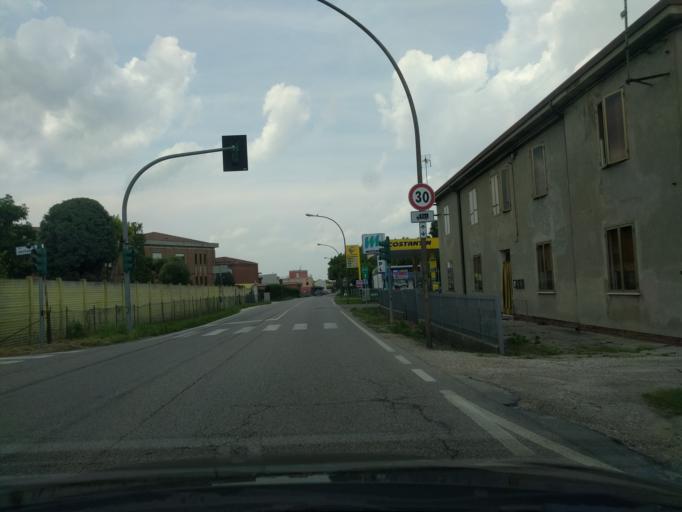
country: IT
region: Veneto
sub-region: Provincia di Rovigo
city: Lendinara
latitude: 45.0846
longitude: 11.6082
